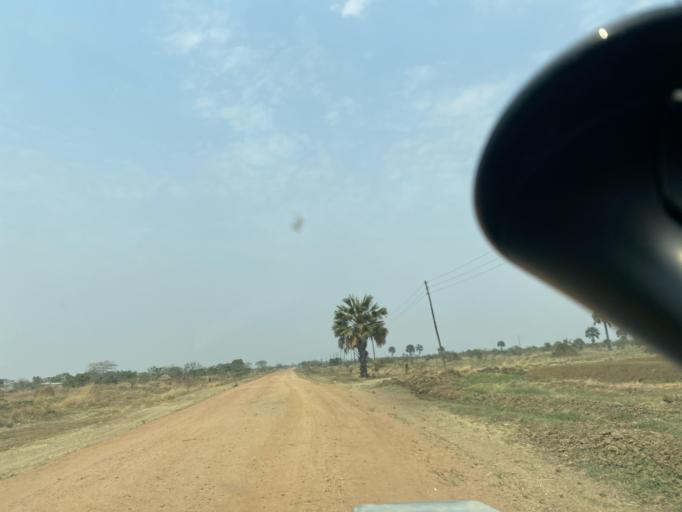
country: ZM
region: Lusaka
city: Kafue
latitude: -15.6746
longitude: 28.0162
